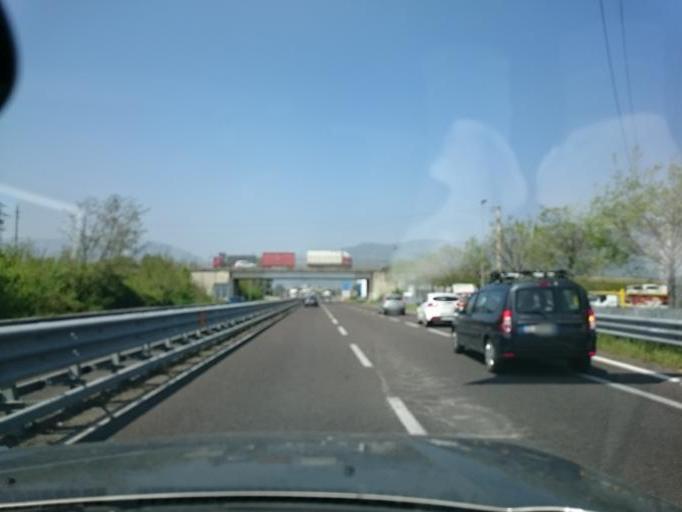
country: IT
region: Veneto
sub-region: Provincia di Vicenza
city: San Zeno-San Giuseppe
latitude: 45.7608
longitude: 11.7718
